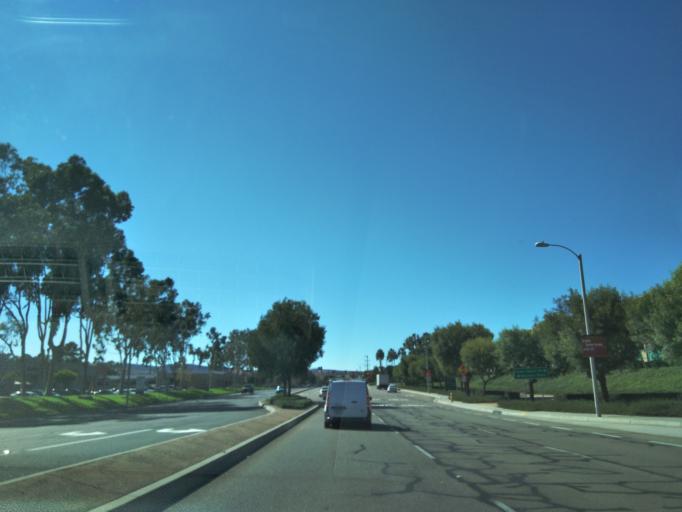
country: US
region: California
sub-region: Orange County
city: Laguna Woods
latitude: 33.6293
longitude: -117.7275
